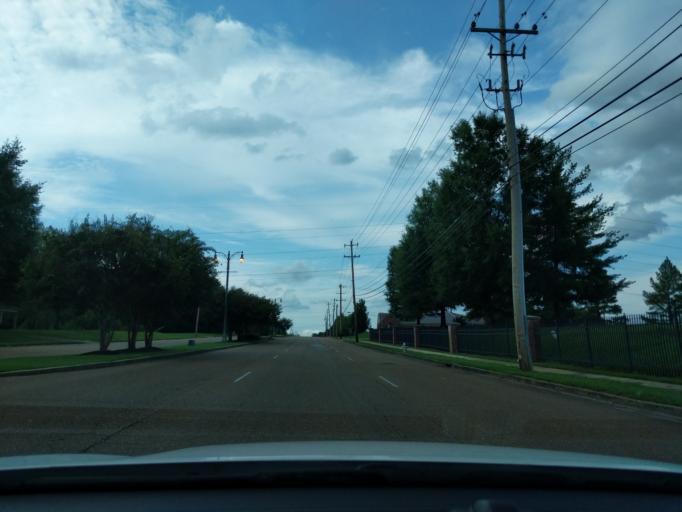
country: US
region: Tennessee
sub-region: Shelby County
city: Germantown
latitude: 35.0390
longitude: -89.7597
